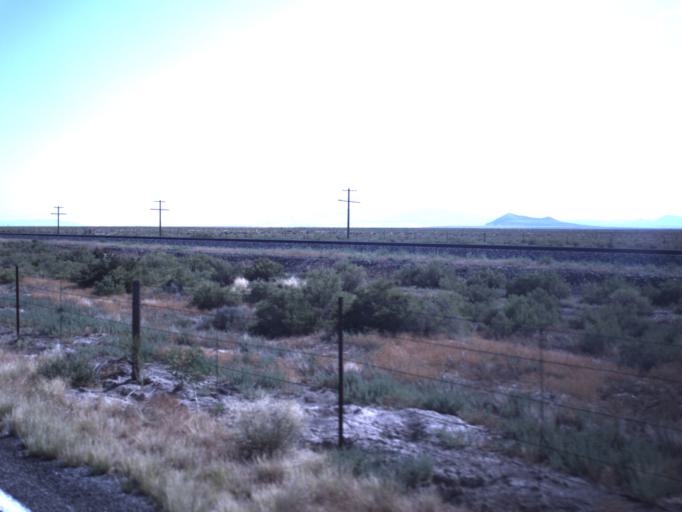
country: US
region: Utah
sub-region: Millard County
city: Delta
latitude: 39.0548
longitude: -112.7657
